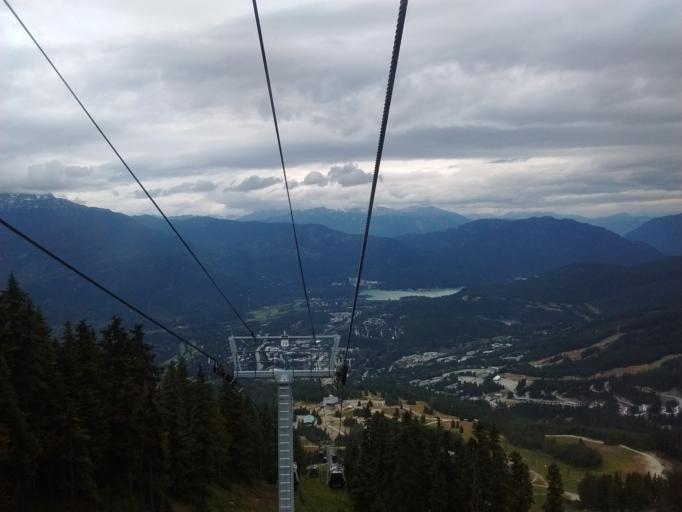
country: CA
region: British Columbia
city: Whistler
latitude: 50.0868
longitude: -122.9497
